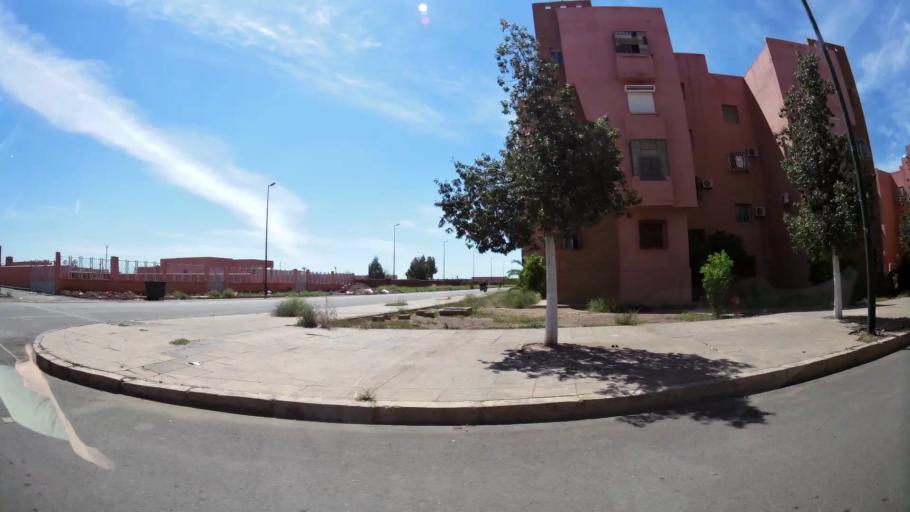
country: MA
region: Marrakech-Tensift-Al Haouz
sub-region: Marrakech
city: Marrakesh
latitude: 31.6339
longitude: -8.0773
